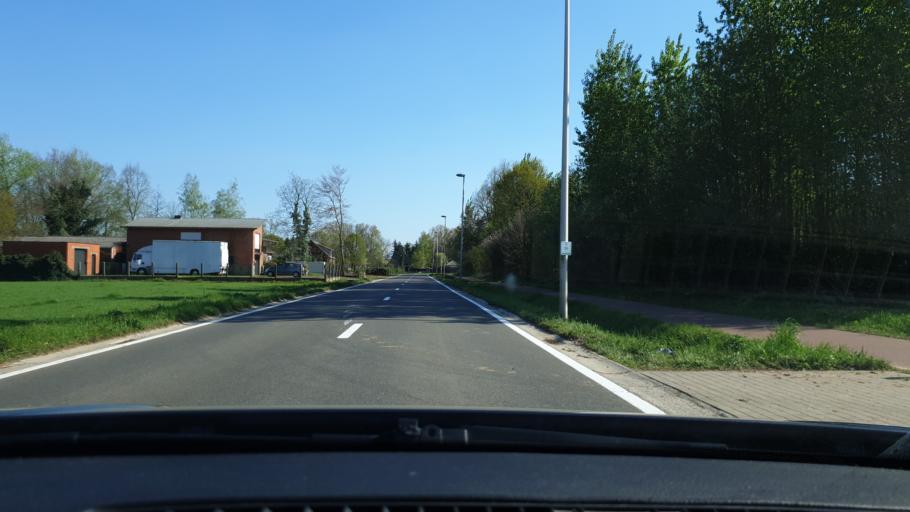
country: BE
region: Flanders
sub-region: Provincie Antwerpen
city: Laakdal
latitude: 51.0892
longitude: 5.0178
